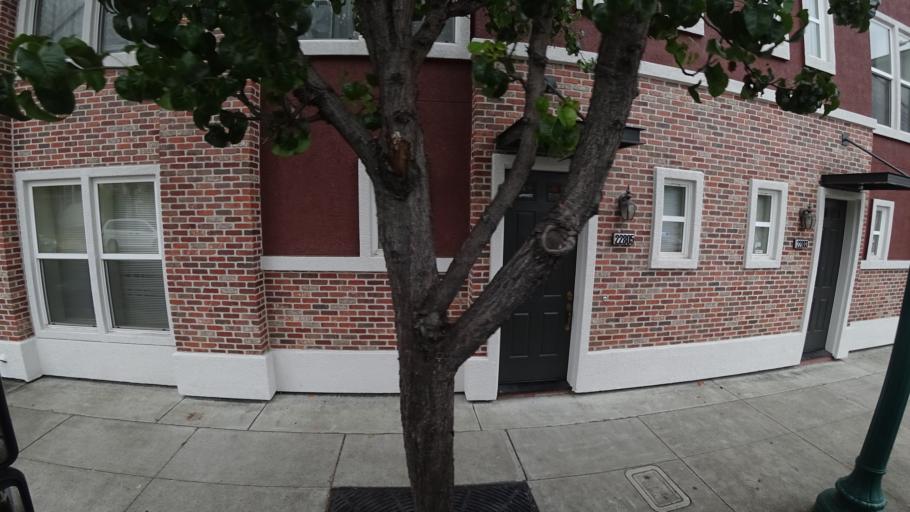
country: US
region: California
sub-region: Alameda County
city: Hayward
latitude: 37.6686
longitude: -122.0837
